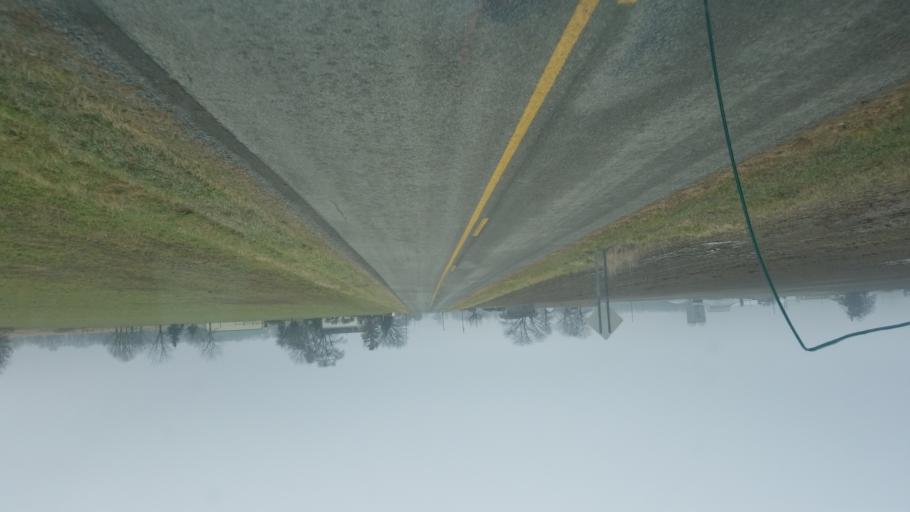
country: US
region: Ohio
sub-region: Champaign County
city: North Lewisburg
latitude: 40.3673
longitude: -83.5471
